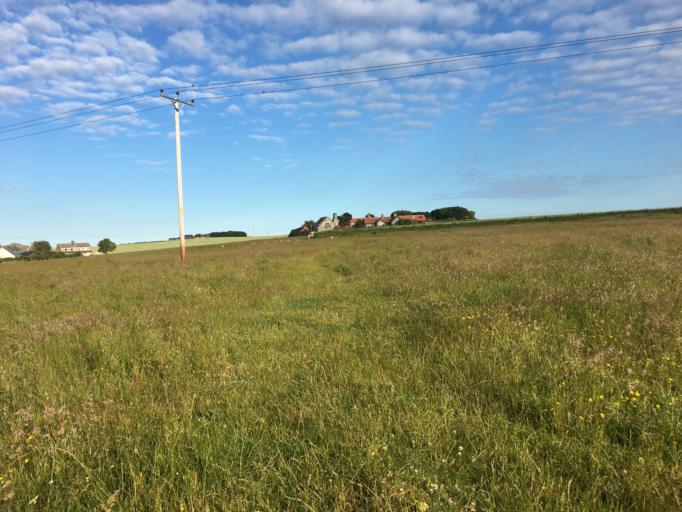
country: GB
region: England
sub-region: Northumberland
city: Bamburgh
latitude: 55.6042
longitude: -1.7039
